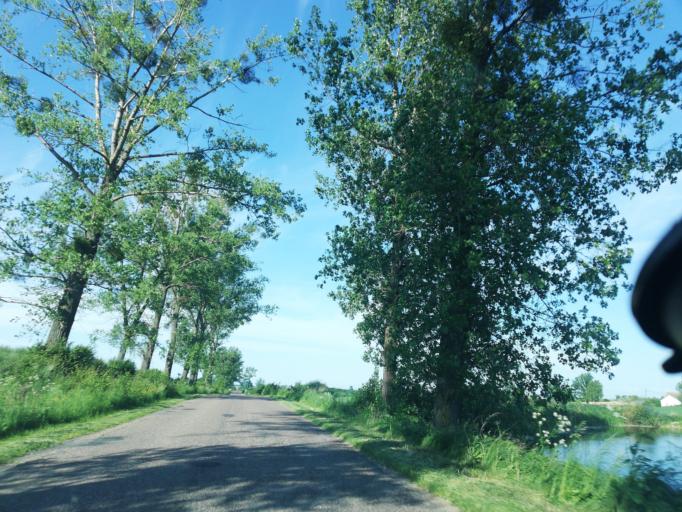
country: PL
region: Kujawsko-Pomorskie
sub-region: Powiat golubsko-dobrzynski
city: Golub-Dobrzyn
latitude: 53.0298
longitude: 19.0701
